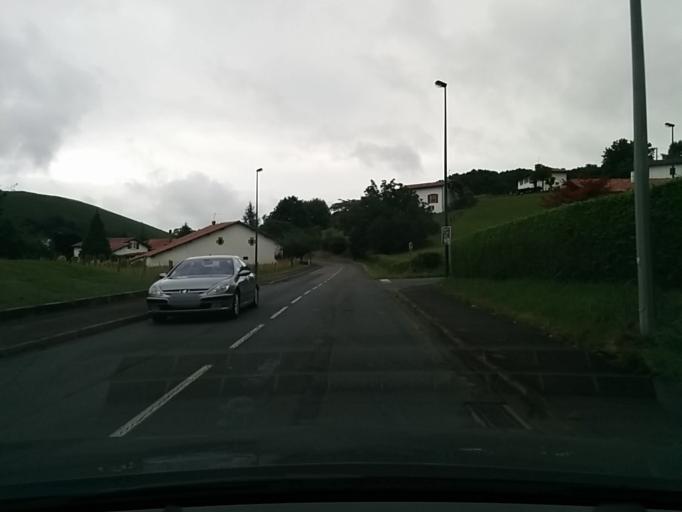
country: FR
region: Aquitaine
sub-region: Departement des Pyrenees-Atlantiques
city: Saint-Pee-sur-Nivelle
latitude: 43.3344
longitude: -1.5483
